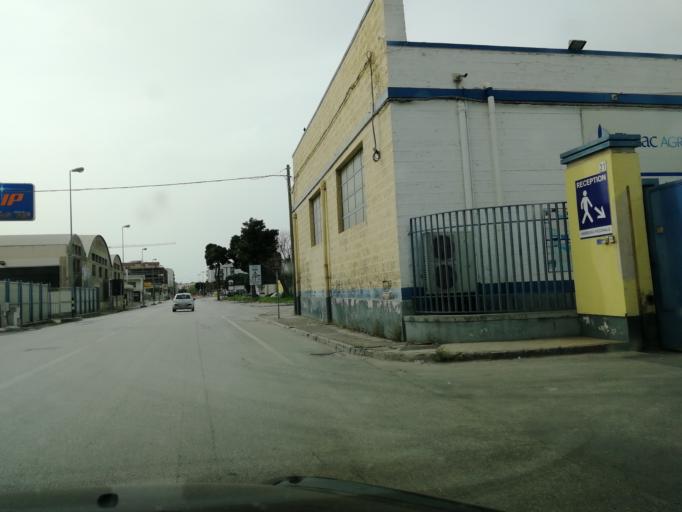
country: IT
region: Apulia
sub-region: Provincia di Barletta - Andria - Trani
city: Barletta
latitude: 41.3173
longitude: 16.2948
